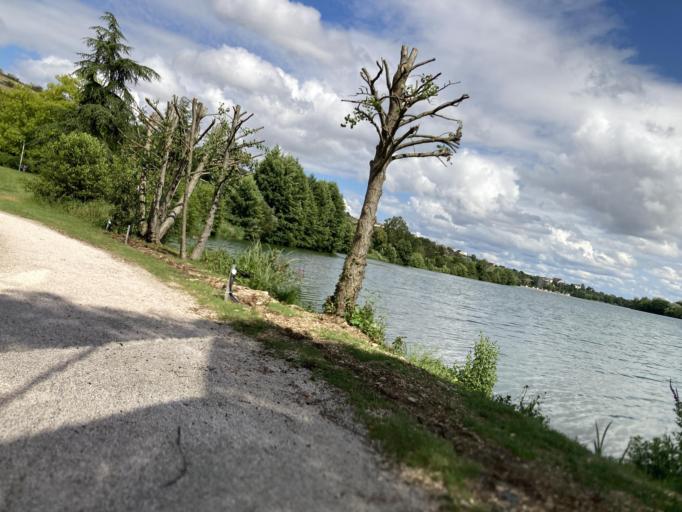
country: FR
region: Bourgogne
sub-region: Departement de la Cote-d'Or
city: Talant
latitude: 47.3301
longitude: 4.9917
